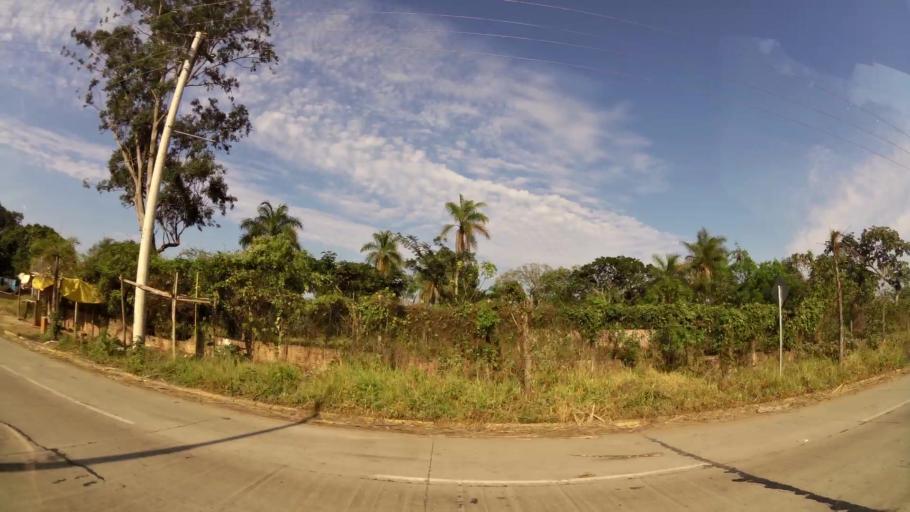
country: BO
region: Santa Cruz
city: Santa Cruz de la Sierra
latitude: -17.7073
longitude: -63.1275
